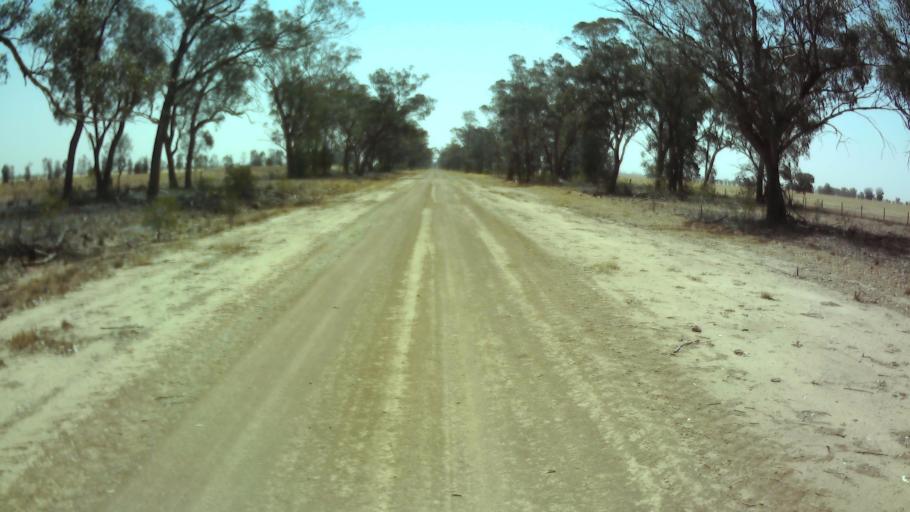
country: AU
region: New South Wales
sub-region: Weddin
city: Grenfell
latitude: -33.9319
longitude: 147.7996
